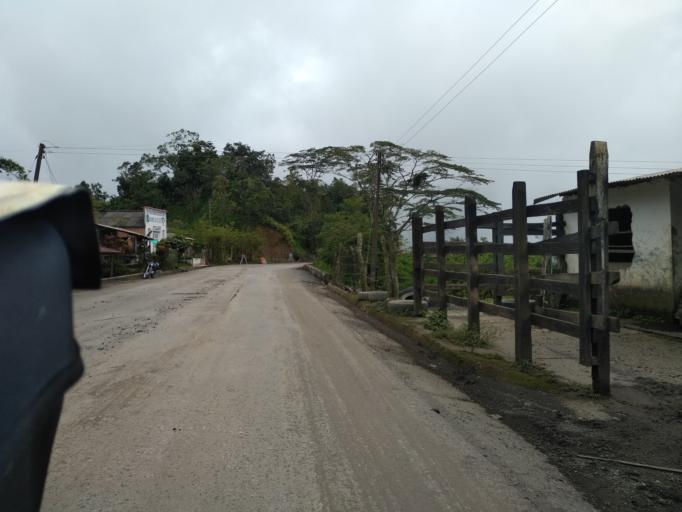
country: CO
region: Santander
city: Landazuri
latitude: 6.1775
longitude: -73.7150
